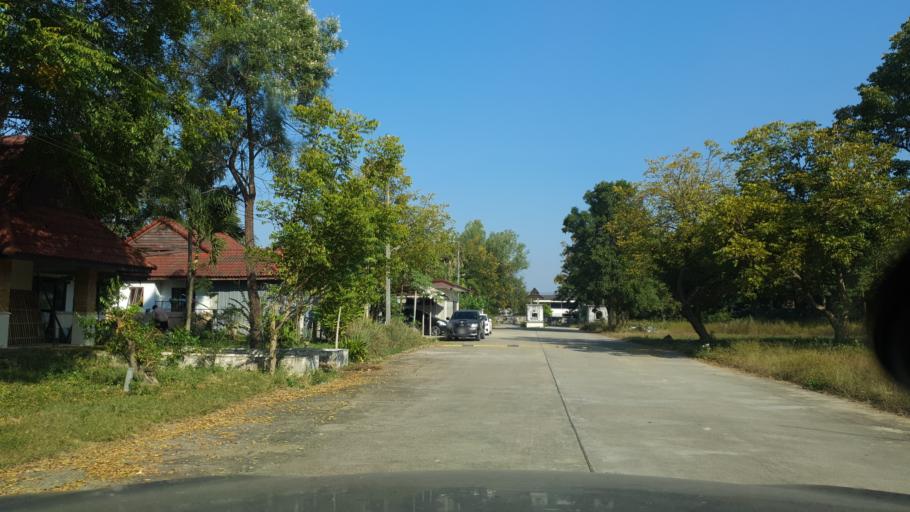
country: TH
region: Lamphun
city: Ban Thi
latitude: 18.6814
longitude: 99.1232
